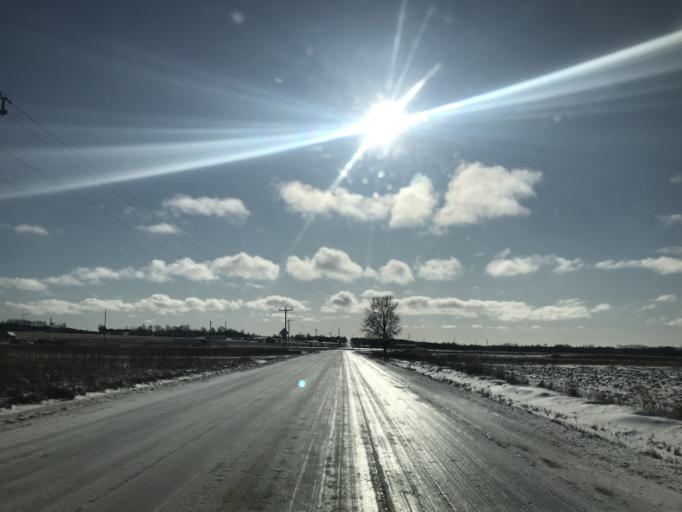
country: US
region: Wisconsin
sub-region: Kewaunee County
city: Luxemburg
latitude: 44.7212
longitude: -87.6208
